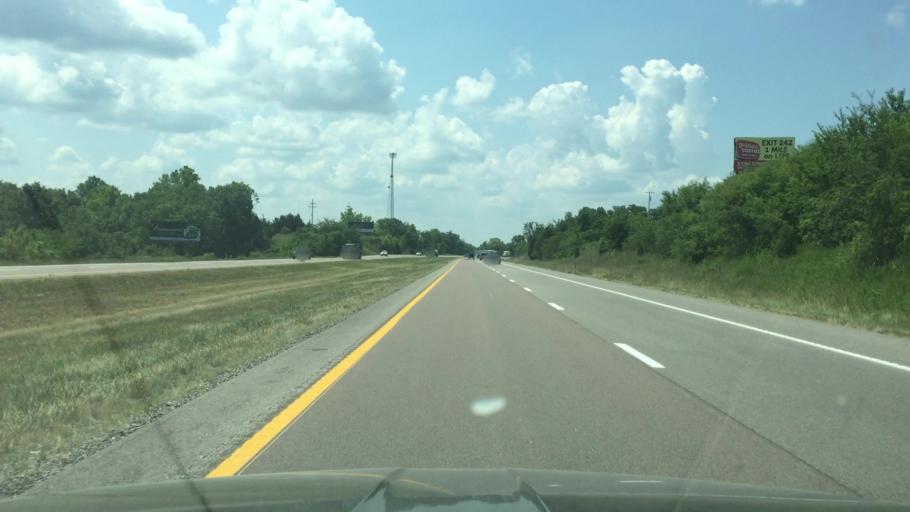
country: US
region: Missouri
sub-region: Miller County
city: Eldon
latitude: 38.2669
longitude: -92.5820
